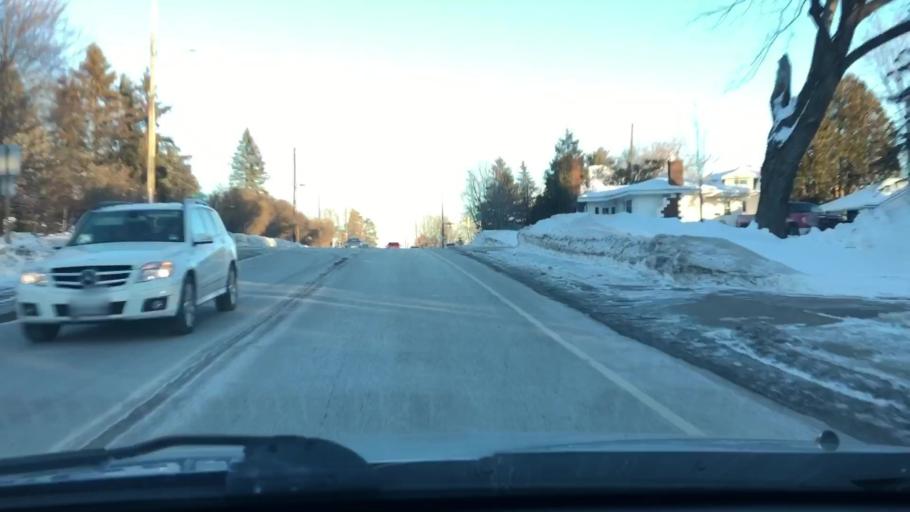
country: US
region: Minnesota
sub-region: Saint Louis County
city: Duluth
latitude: 46.8258
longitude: -92.0734
